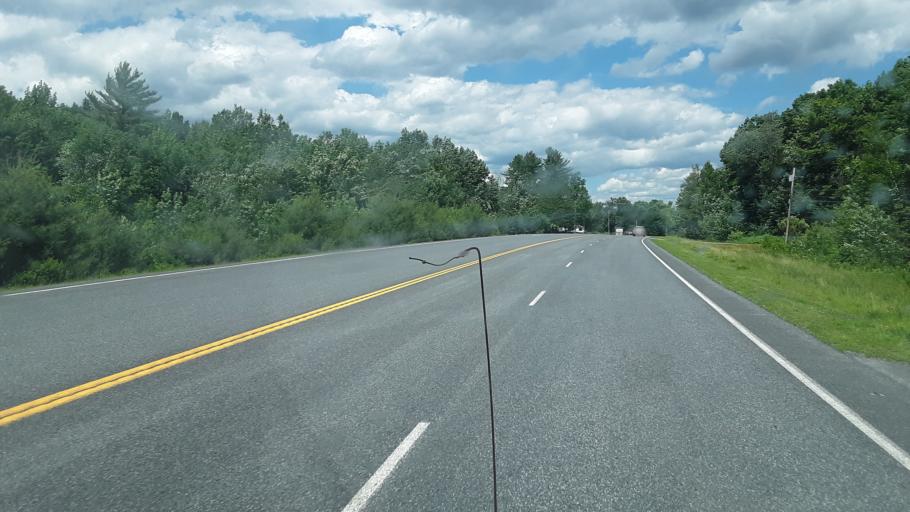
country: US
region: Maine
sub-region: Franklin County
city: Wilton
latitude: 44.5881
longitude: -70.2820
